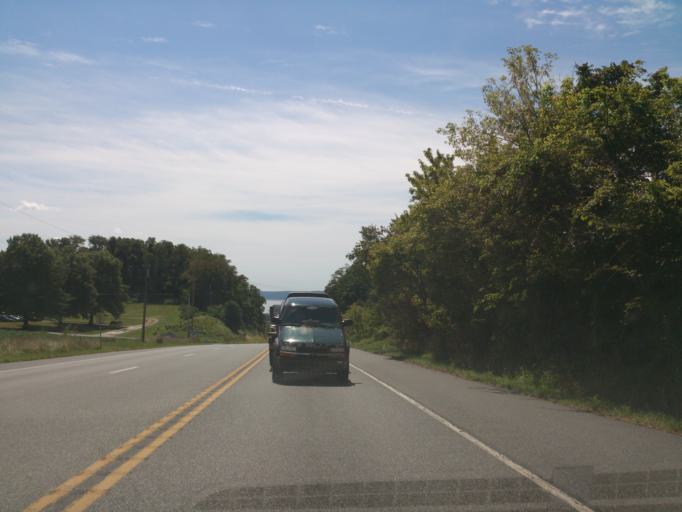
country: US
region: Pennsylvania
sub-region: Lancaster County
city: Columbia
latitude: 40.0446
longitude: -76.5134
